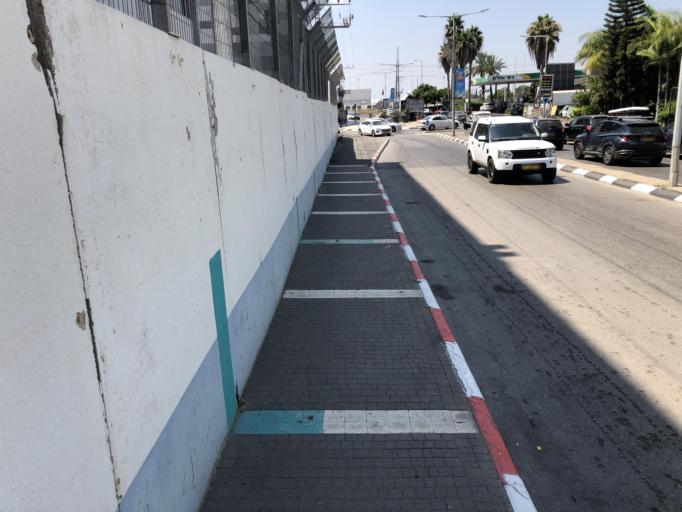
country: IL
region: Central District
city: Yehud
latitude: 32.0271
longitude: 34.8987
